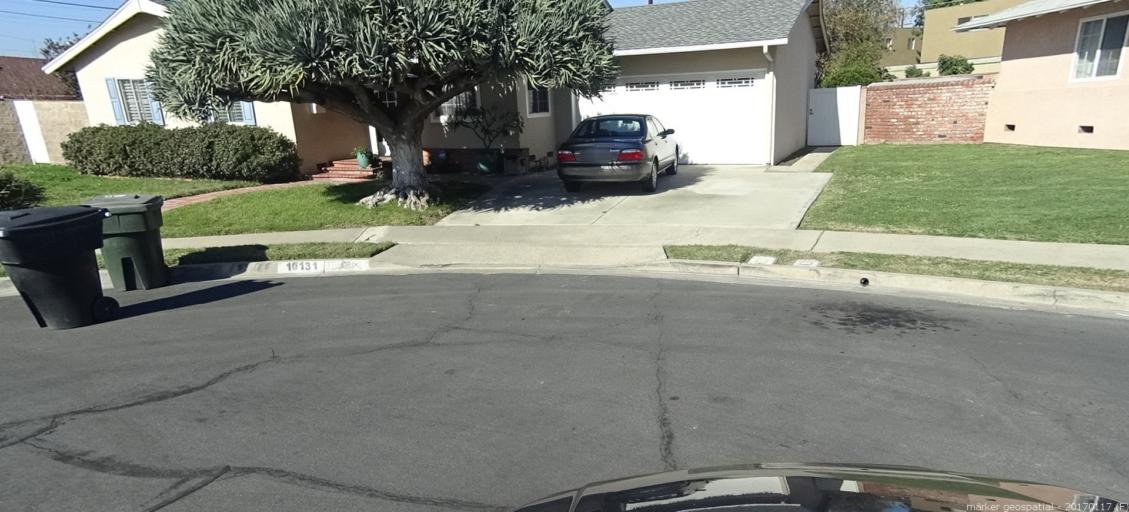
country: US
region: California
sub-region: Orange County
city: Stanton
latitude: 33.8156
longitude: -117.9668
